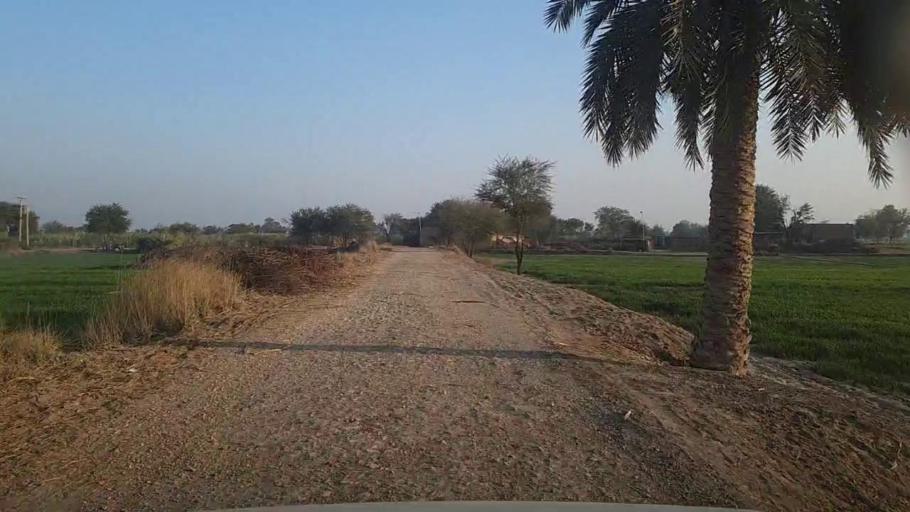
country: PK
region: Sindh
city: Khairpur
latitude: 28.0610
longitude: 69.7550
